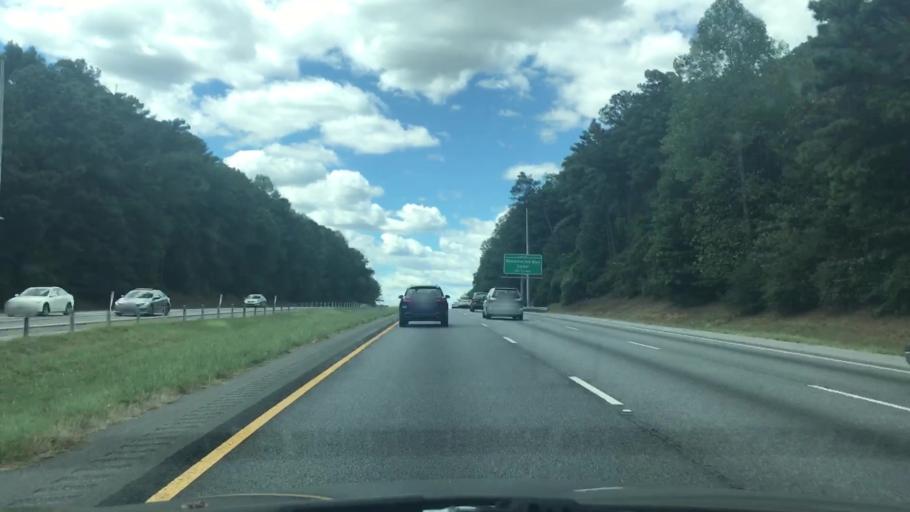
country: US
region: Georgia
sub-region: DeKalb County
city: Stone Mountain
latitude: 33.8328
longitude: -84.1876
